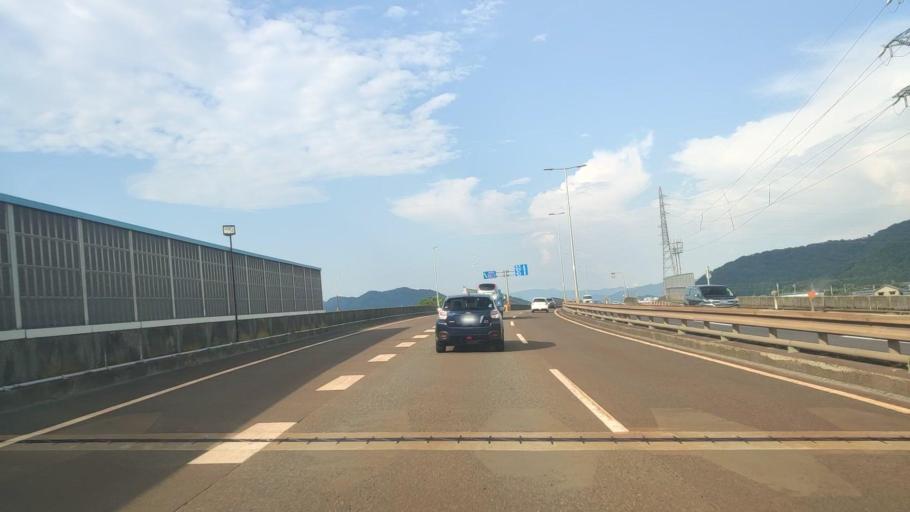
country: JP
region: Fukui
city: Takefu
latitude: 35.8751
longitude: 136.1624
